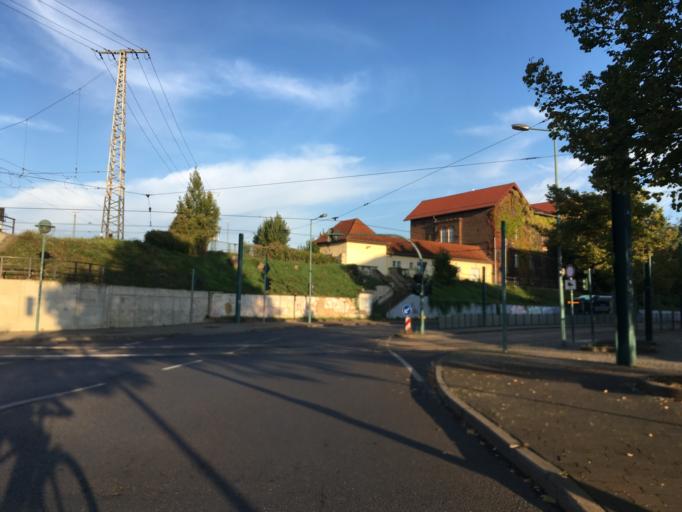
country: DE
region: Brandenburg
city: Frankfurt (Oder)
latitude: 52.3379
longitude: 14.5460
